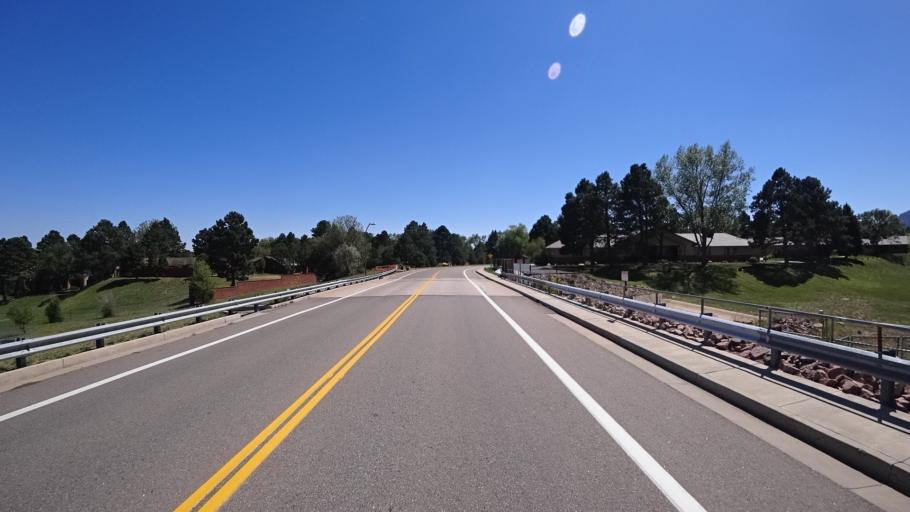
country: US
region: Colorado
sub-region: El Paso County
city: Colorado Springs
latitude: 38.7937
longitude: -104.8283
